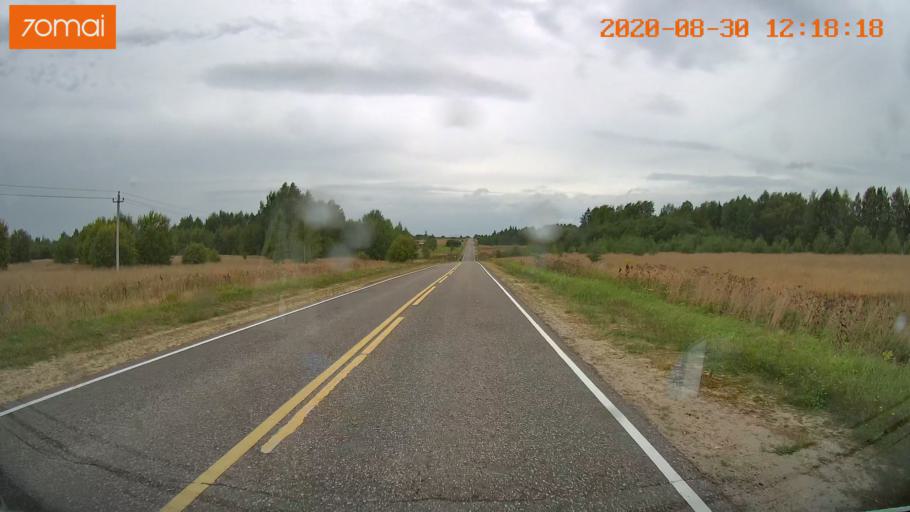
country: RU
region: Ivanovo
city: Yur'yevets
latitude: 57.3234
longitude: 42.9558
